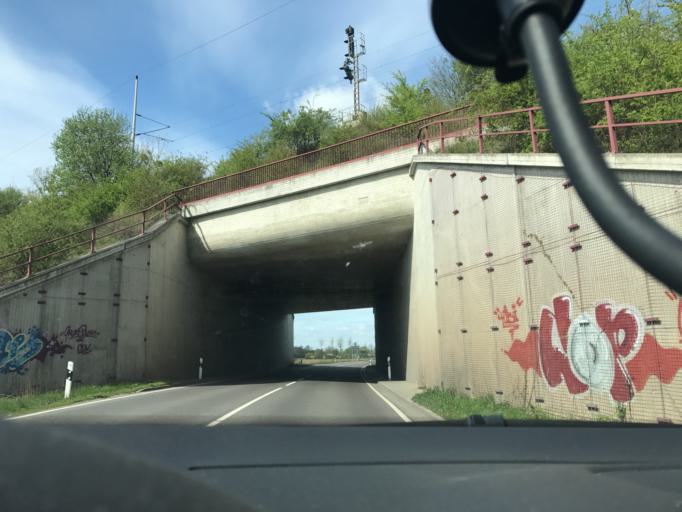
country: DE
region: Lower Saxony
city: Helmstedt
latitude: 52.2162
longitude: 10.9996
